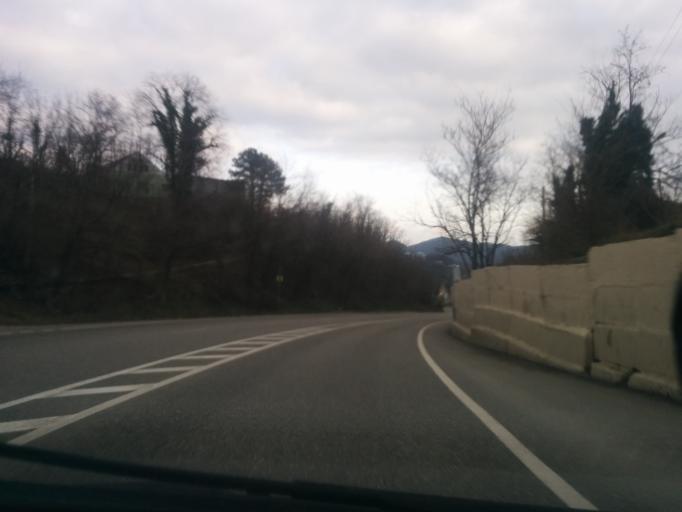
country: RU
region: Krasnodarskiy
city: Nebug
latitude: 44.1663
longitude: 38.9913
